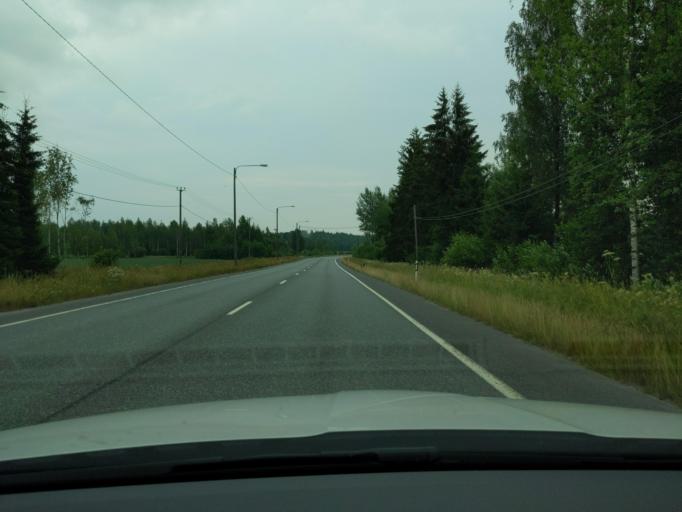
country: FI
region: Uusimaa
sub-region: Helsinki
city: Pornainen
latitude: 60.3449
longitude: 25.4478
